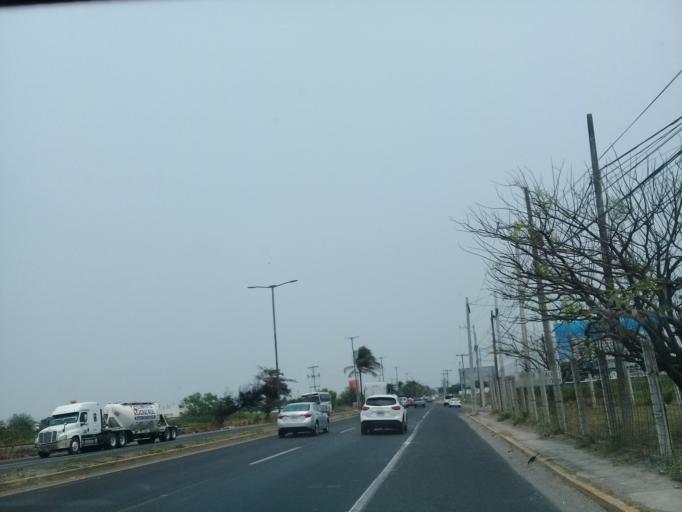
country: MX
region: Veracruz
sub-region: Veracruz
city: Hacienda Sotavento
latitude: 19.1493
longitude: -96.1727
